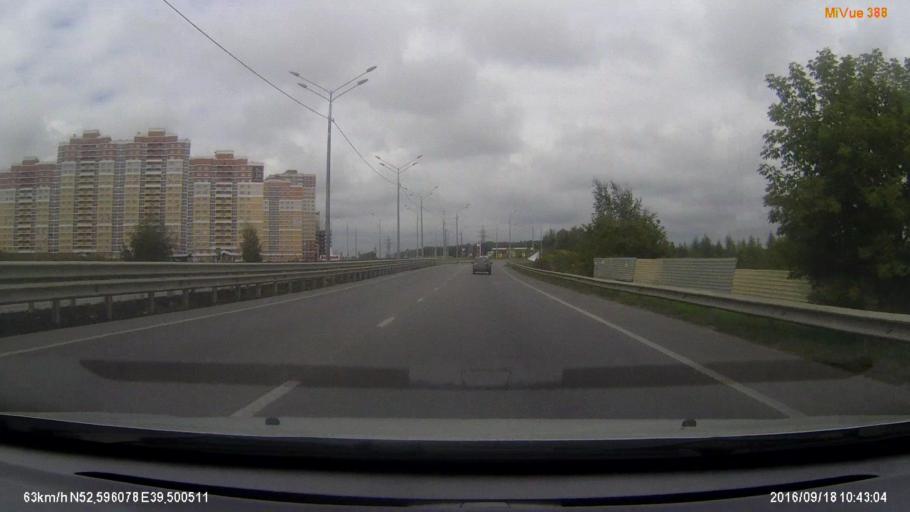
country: RU
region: Lipetsk
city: Syrskoye
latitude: 52.5959
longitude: 39.5007
